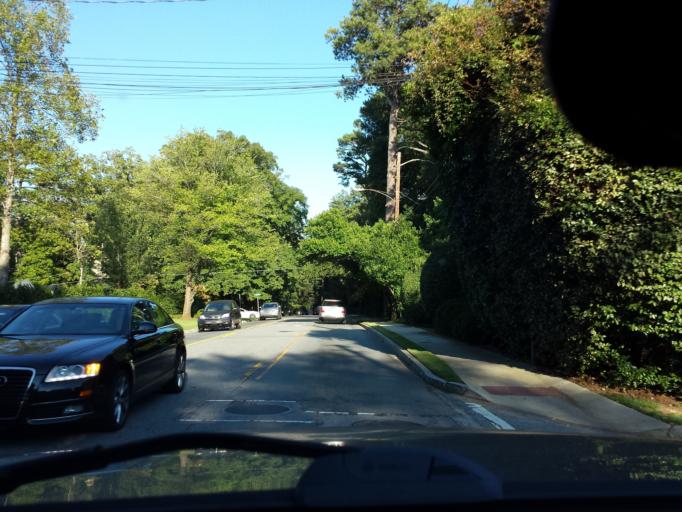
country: US
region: Georgia
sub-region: DeKalb County
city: North Atlanta
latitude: 33.8441
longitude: -84.3938
